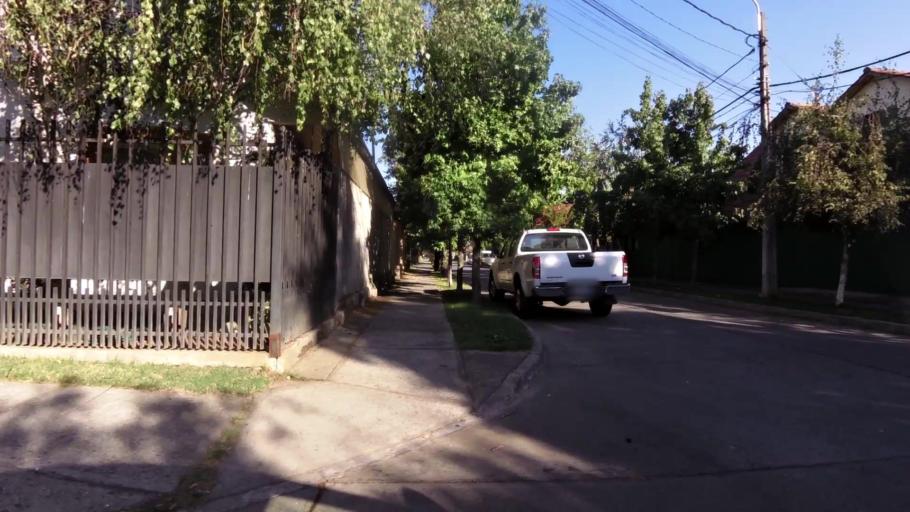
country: CL
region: Maule
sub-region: Provincia de Talca
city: Talca
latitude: -35.4402
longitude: -71.6870
